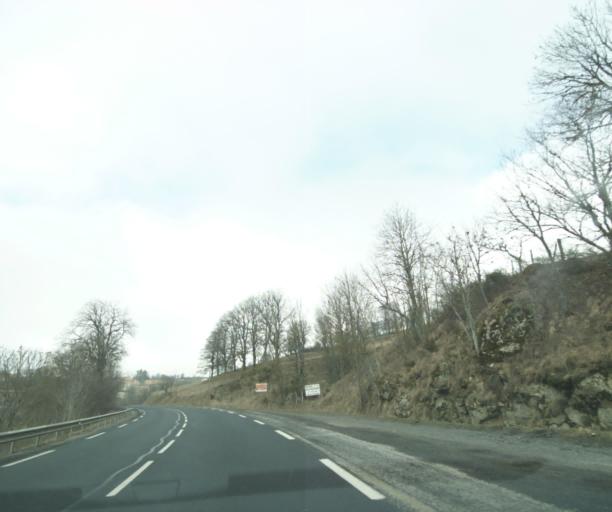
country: FR
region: Languedoc-Roussillon
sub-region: Departement de la Lozere
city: Langogne
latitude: 44.7649
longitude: 3.8854
